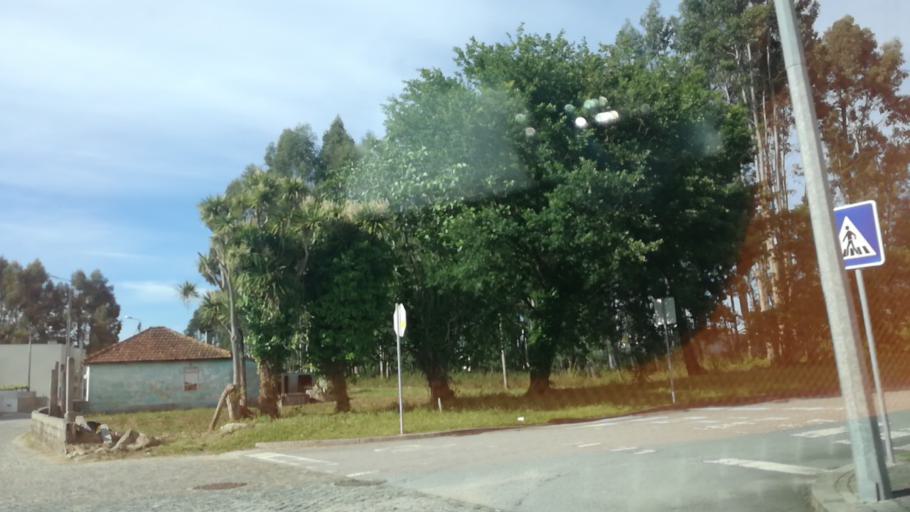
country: PT
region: Porto
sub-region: Maia
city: Nogueira
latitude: 41.2421
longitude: -8.5938
